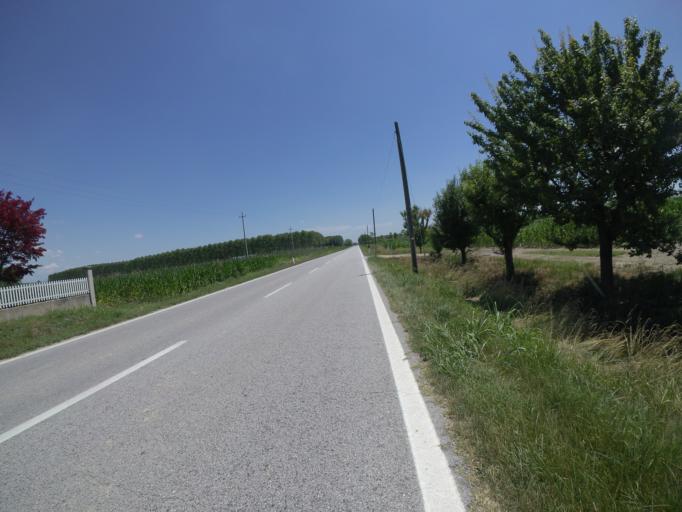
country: IT
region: Friuli Venezia Giulia
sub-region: Provincia di Udine
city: Rivignano
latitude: 45.8815
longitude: 13.0193
